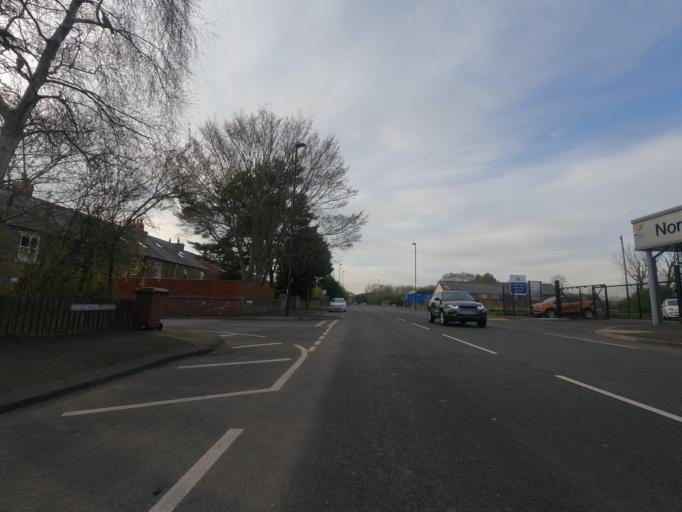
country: GB
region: England
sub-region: Newcastle upon Tyne
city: Hazlerigg
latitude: 55.0614
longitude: -1.6297
